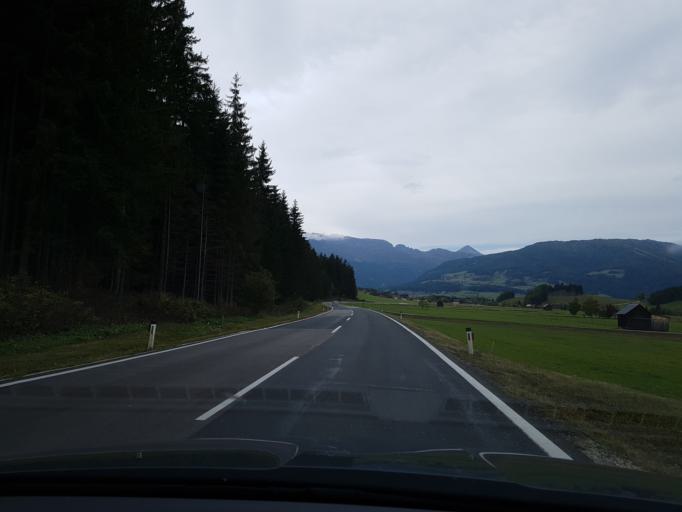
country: AT
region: Salzburg
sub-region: Politischer Bezirk Tamsweg
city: Mariapfarr
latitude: 47.1394
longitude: 13.7619
